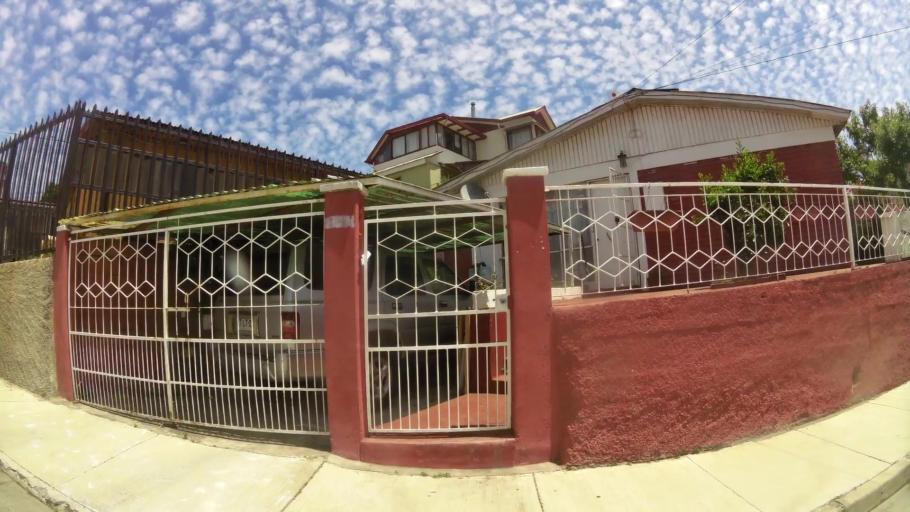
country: CL
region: Valparaiso
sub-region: Provincia de Valparaiso
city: Vina del Mar
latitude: -33.0452
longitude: -71.5759
